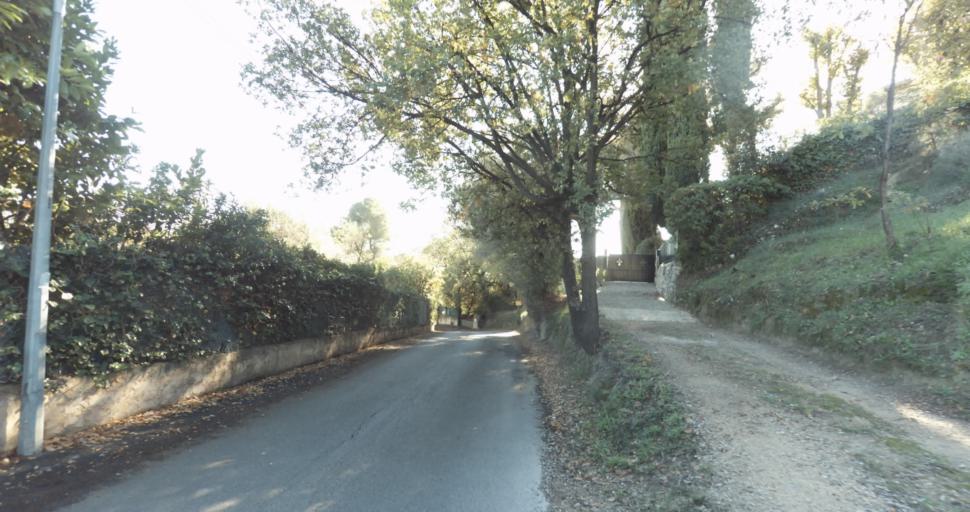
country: FR
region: Provence-Alpes-Cote d'Azur
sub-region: Departement des Alpes-Maritimes
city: Saint-Paul-de-Vence
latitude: 43.6982
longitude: 7.1364
